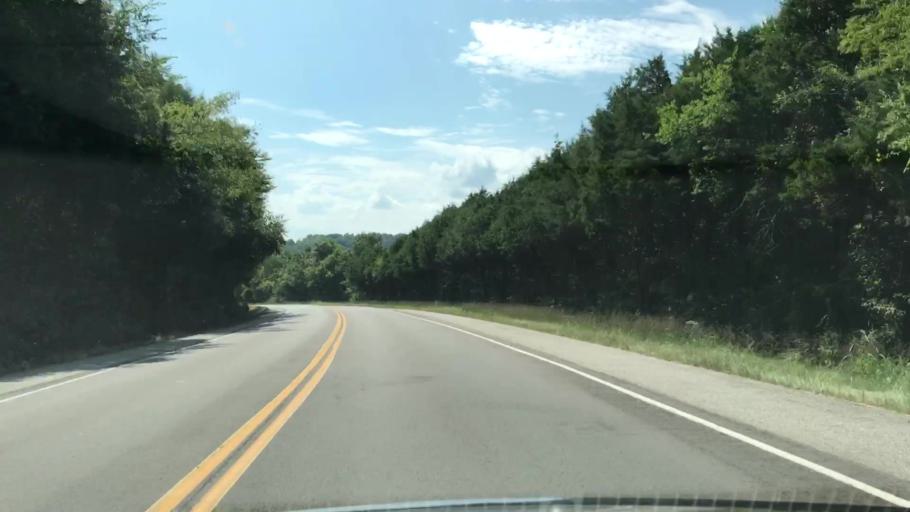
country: US
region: Tennessee
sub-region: Smith County
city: Carthage
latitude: 36.3268
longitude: -86.0221
